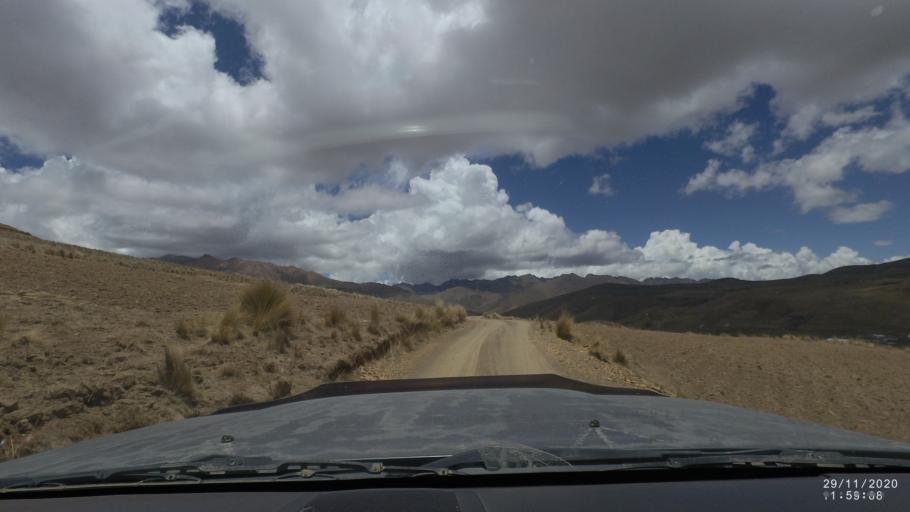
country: BO
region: Cochabamba
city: Cochabamba
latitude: -17.1547
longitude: -66.2775
